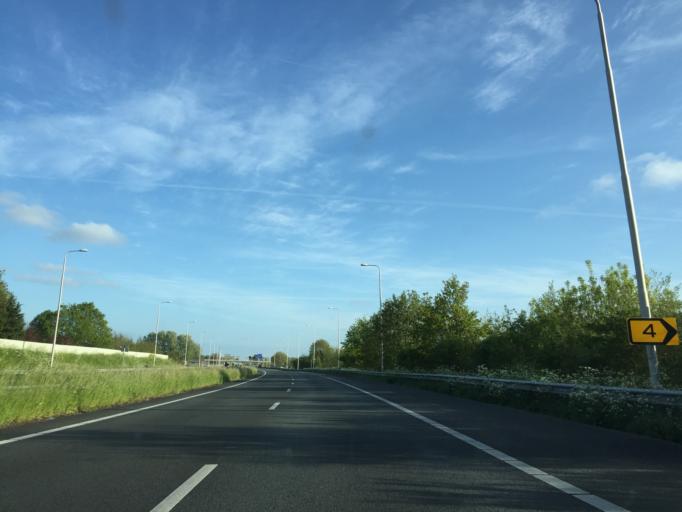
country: NL
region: North Holland
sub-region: Gemeente Hoorn
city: Hoorn
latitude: 52.6764
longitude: 5.0306
